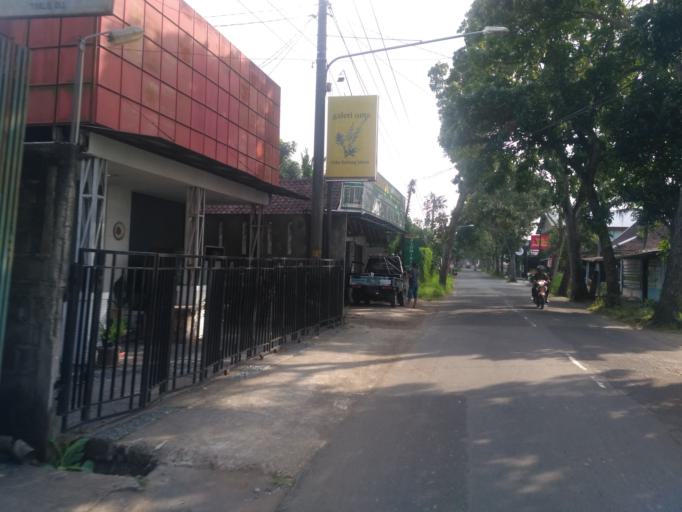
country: ID
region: Daerah Istimewa Yogyakarta
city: Yogyakarta
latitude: -7.7765
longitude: 110.3417
